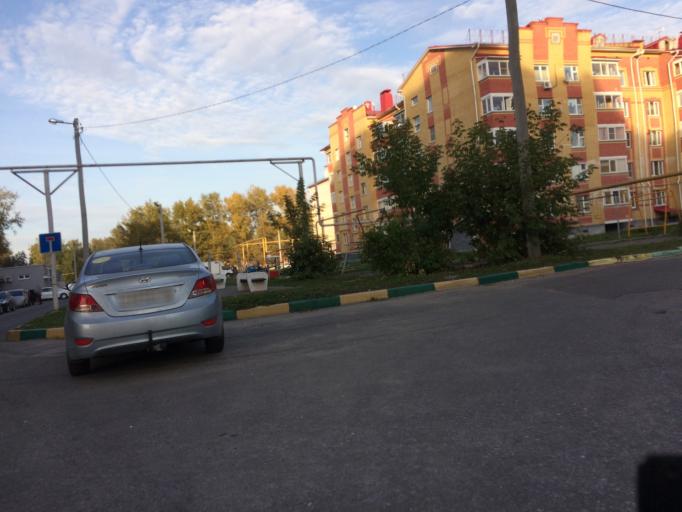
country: RU
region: Mariy-El
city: Yoshkar-Ola
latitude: 56.6299
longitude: 47.8502
